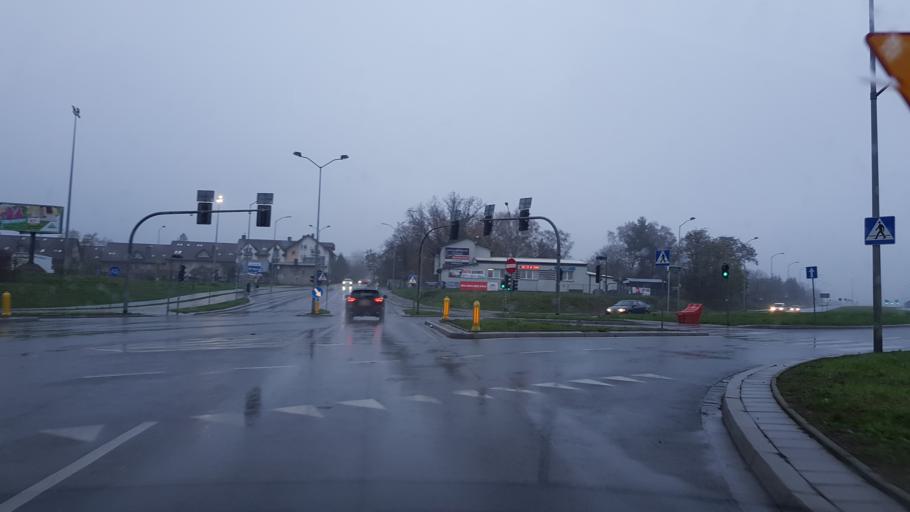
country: PL
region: West Pomeranian Voivodeship
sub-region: Szczecin
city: Szczecin
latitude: 53.4618
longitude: 14.5553
